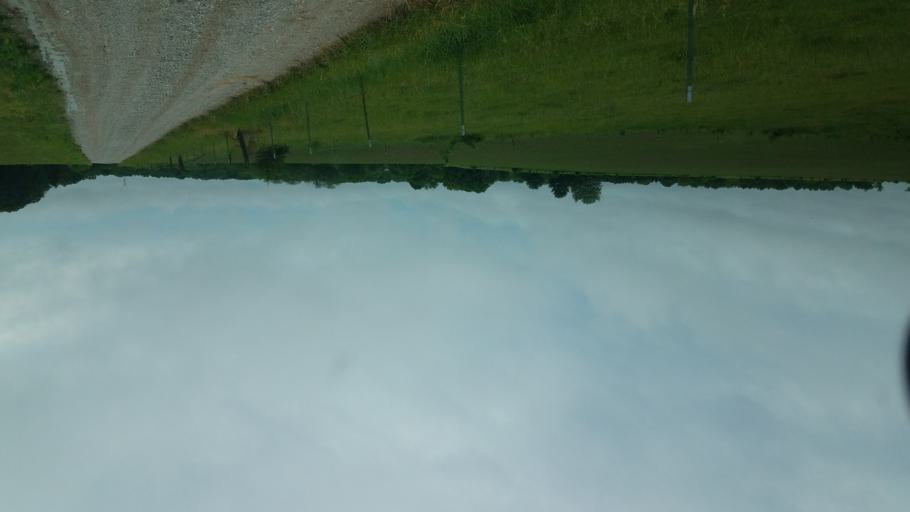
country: US
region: Missouri
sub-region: Cooper County
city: Boonville
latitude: 38.8559
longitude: -92.6460
